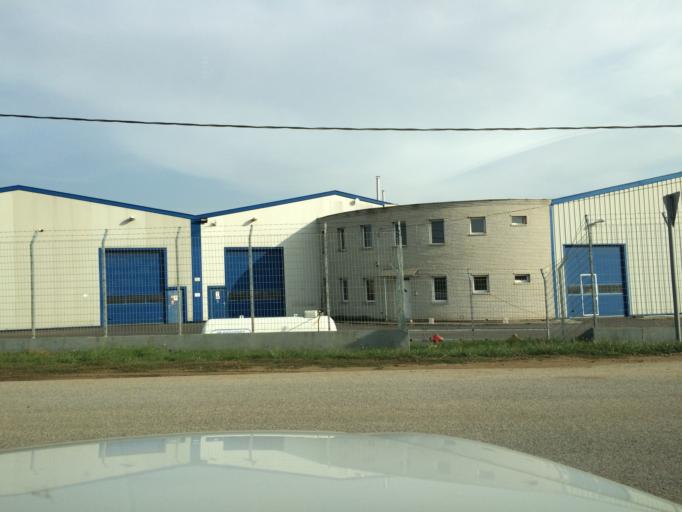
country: HU
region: Szabolcs-Szatmar-Bereg
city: Nyirtelek
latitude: 47.9538
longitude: 21.6504
